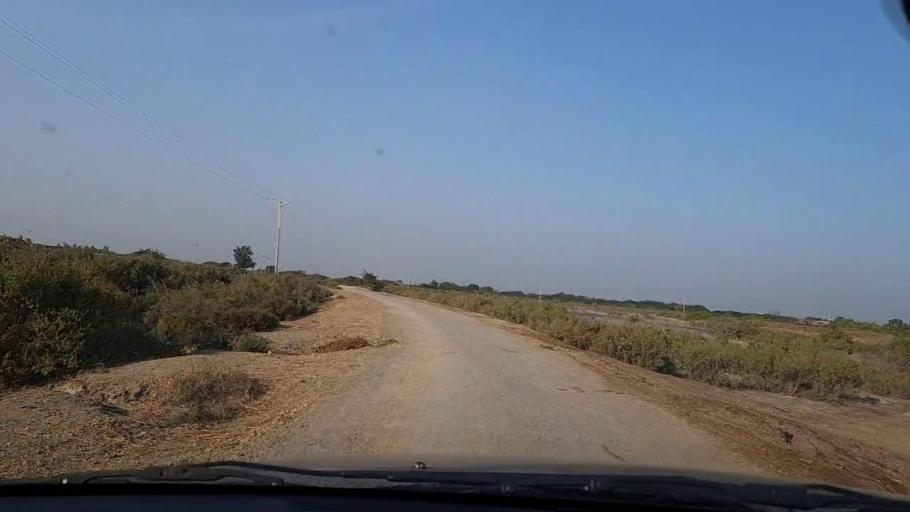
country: PK
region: Sindh
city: Chuhar Jamali
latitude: 24.2914
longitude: 67.7550
